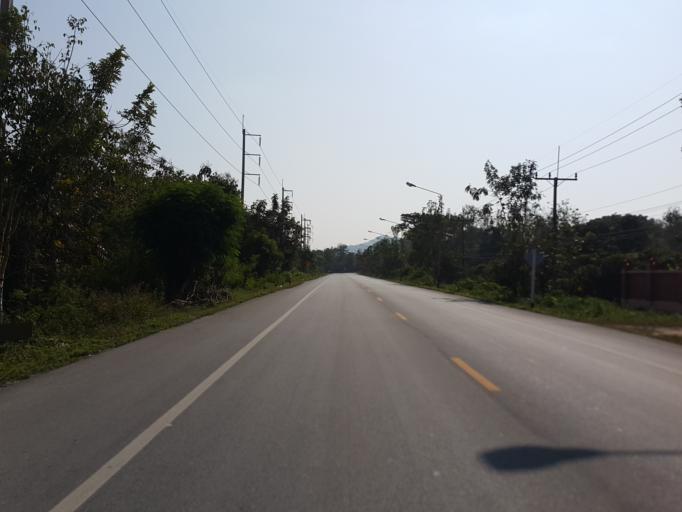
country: TH
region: Lampang
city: Chae Hom
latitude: 18.6553
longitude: 99.5385
